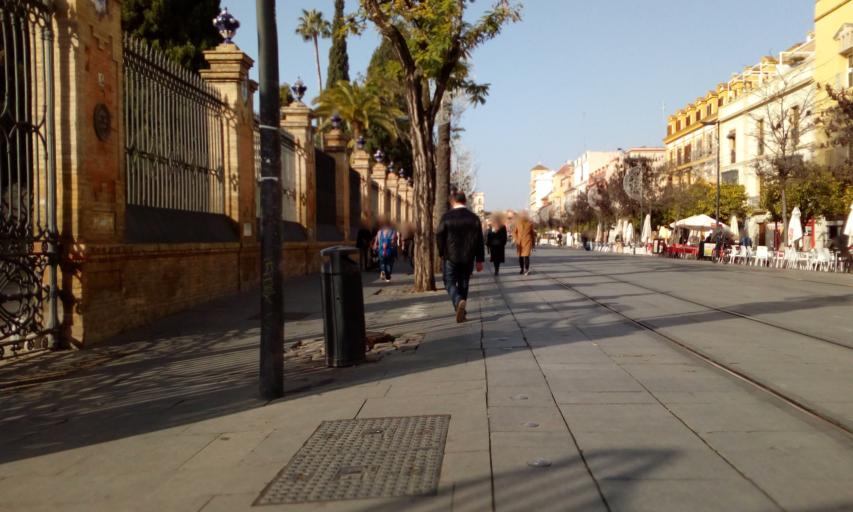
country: ES
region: Andalusia
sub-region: Provincia de Sevilla
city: Sevilla
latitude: 37.3817
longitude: -5.9905
